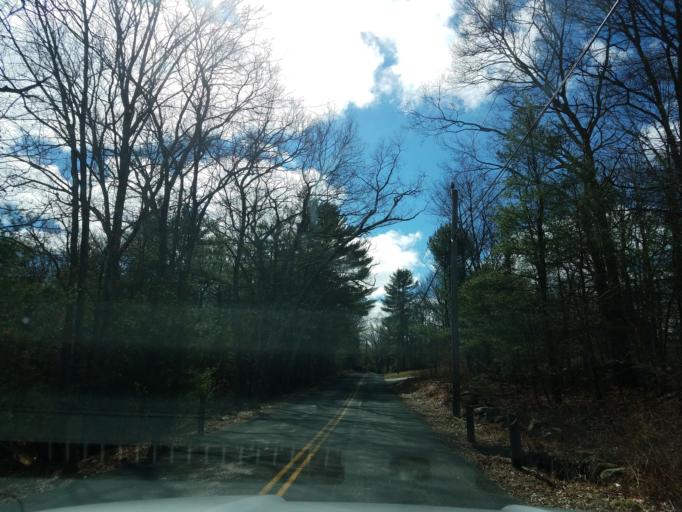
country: US
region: Connecticut
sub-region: Windham County
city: North Grosvenor Dale
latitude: 42.0144
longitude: -71.9150
